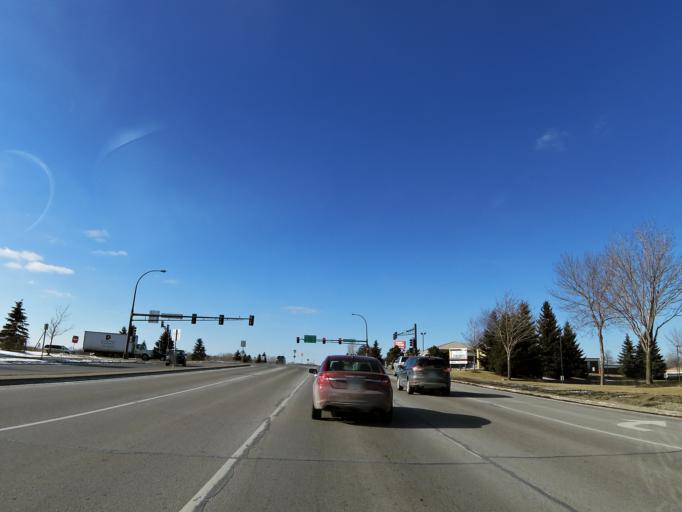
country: US
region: Minnesota
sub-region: Washington County
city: Woodbury
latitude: 44.9142
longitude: -92.9768
